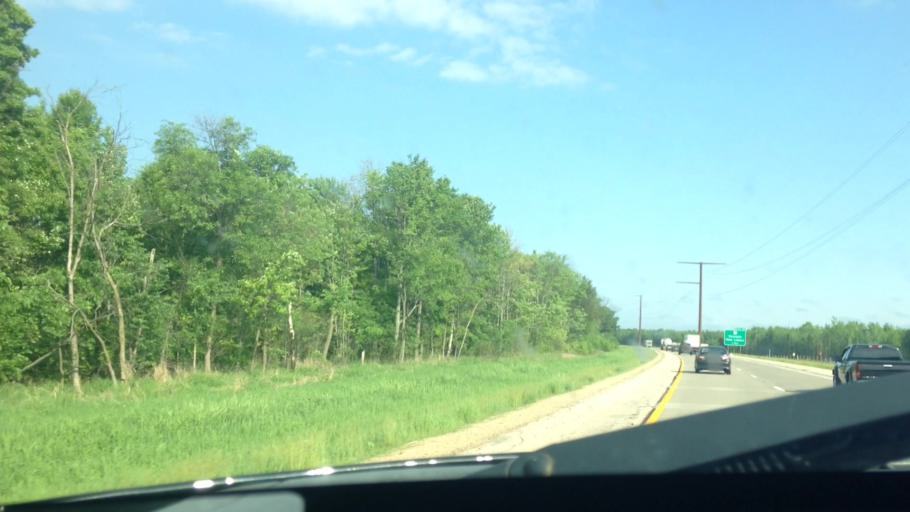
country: US
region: Wisconsin
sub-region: Juneau County
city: New Lisbon
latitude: 43.8696
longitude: -90.1233
